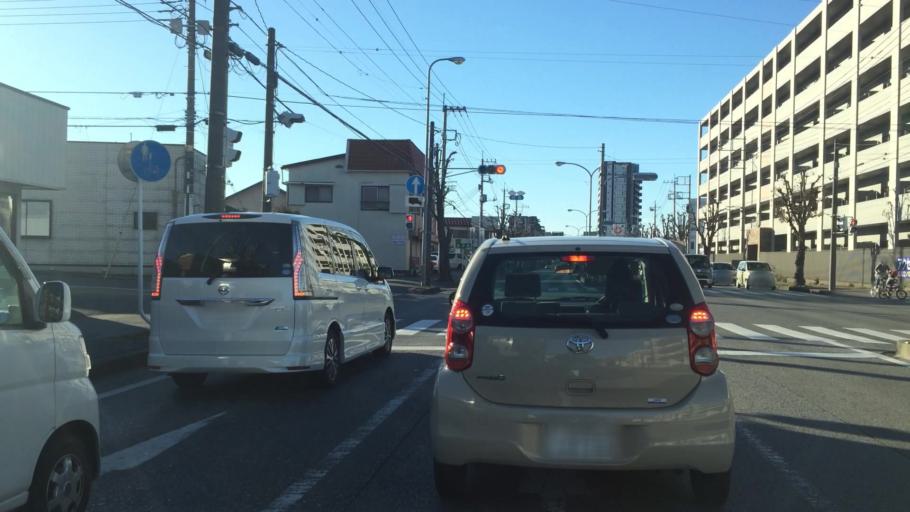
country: JP
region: Tochigi
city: Utsunomiya-shi
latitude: 36.5573
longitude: 139.9230
